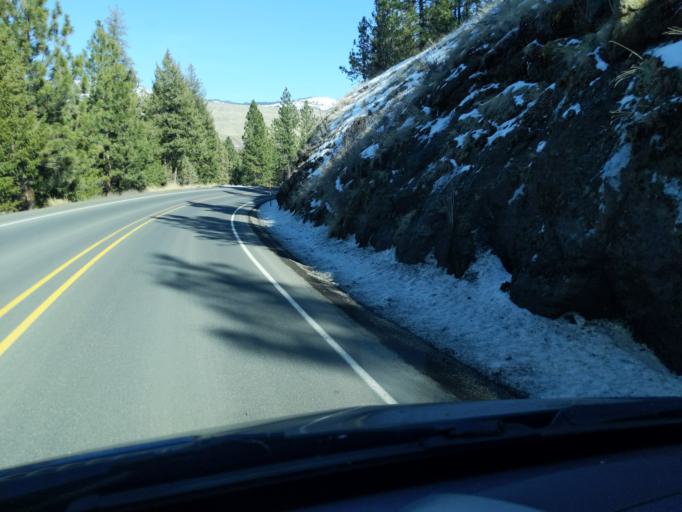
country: US
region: Oregon
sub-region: Grant County
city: John Day
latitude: 44.8359
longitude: -119.0382
